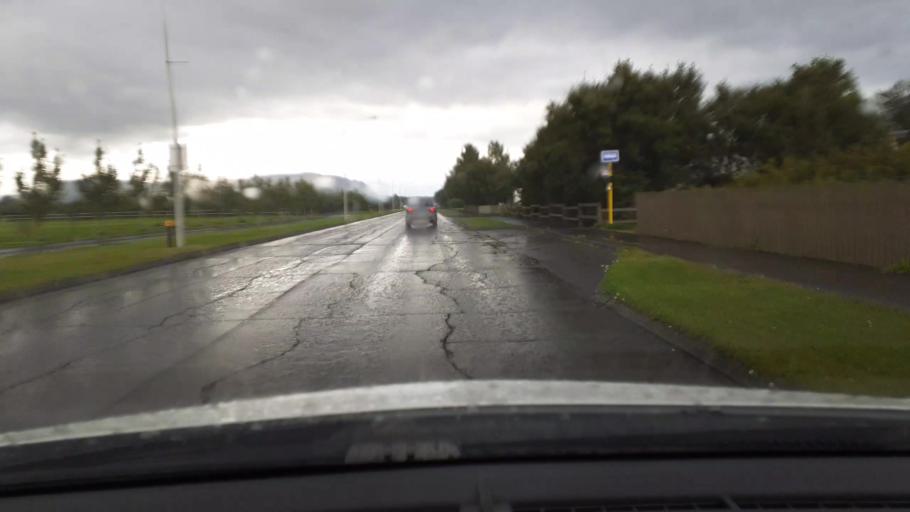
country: IS
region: West
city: Akranes
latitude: 64.3190
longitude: -22.0492
